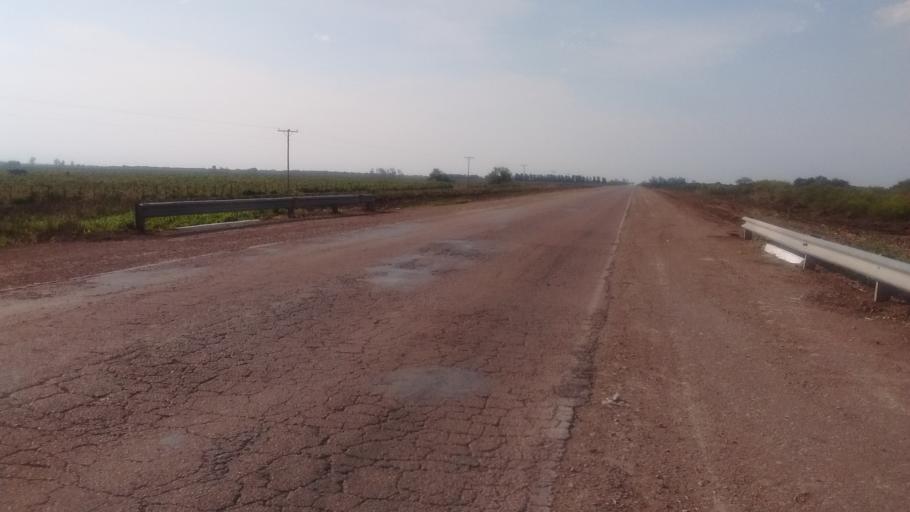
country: AR
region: Santiago del Estero
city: Los Juries
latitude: -28.6278
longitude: -61.5222
